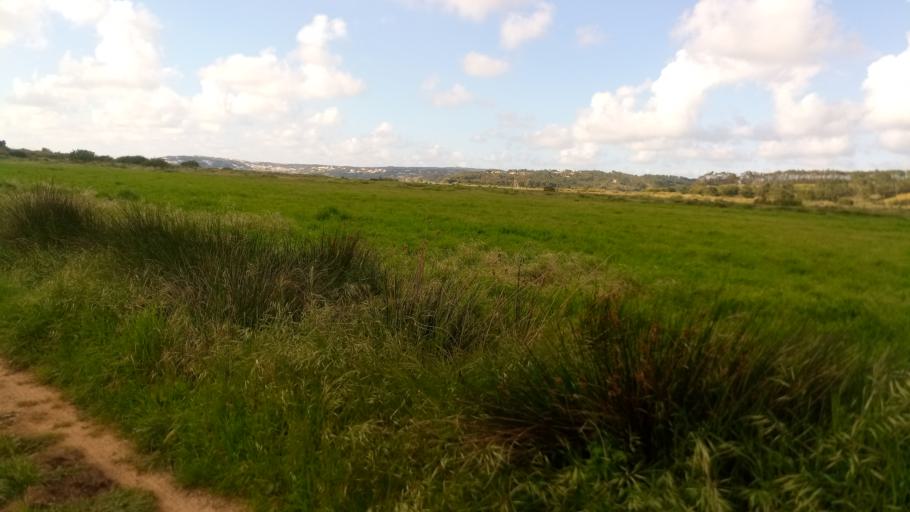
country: PT
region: Leiria
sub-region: Obidos
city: Obidos
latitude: 39.3922
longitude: -9.2004
